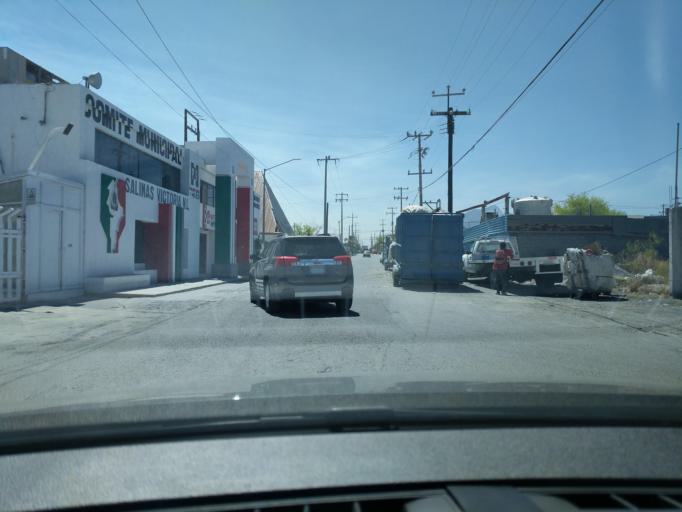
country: MX
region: Nuevo Leon
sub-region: Salinas Victoria
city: Las Torres
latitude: 25.9646
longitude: -100.2965
